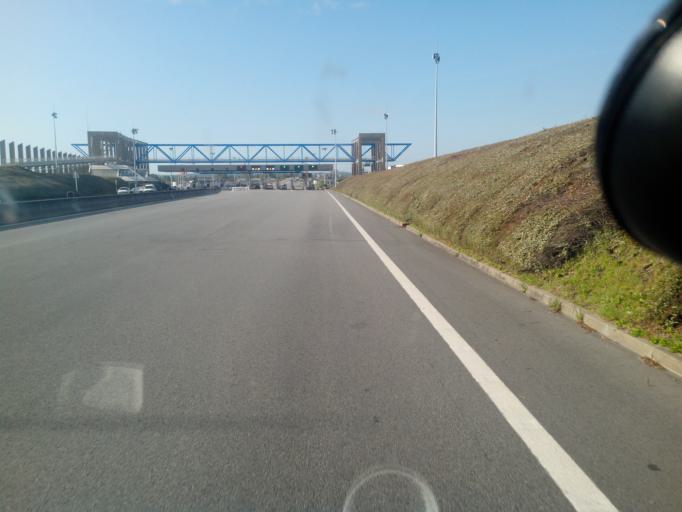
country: FR
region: Lower Normandy
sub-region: Departement du Calvados
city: La Riviere-Saint-Sauveur
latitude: 49.4480
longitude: 0.2720
